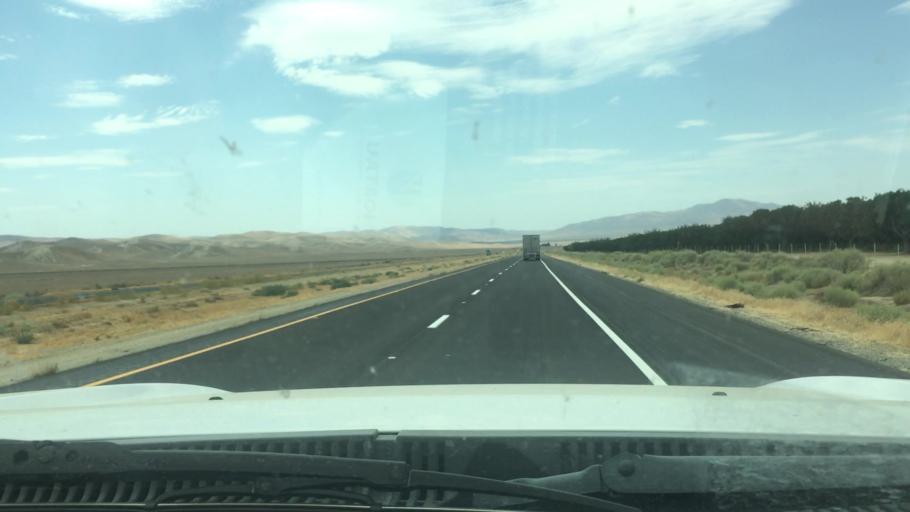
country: US
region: California
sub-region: Kern County
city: Lost Hills
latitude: 35.6157
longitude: -119.9669
